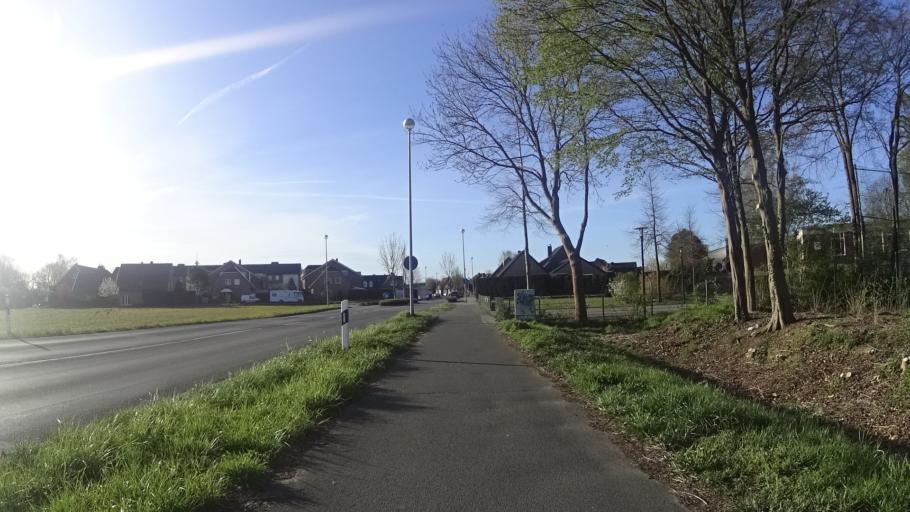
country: DE
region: North Rhine-Westphalia
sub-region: Regierungsbezirk Munster
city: Greven
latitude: 52.1021
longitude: 7.5876
